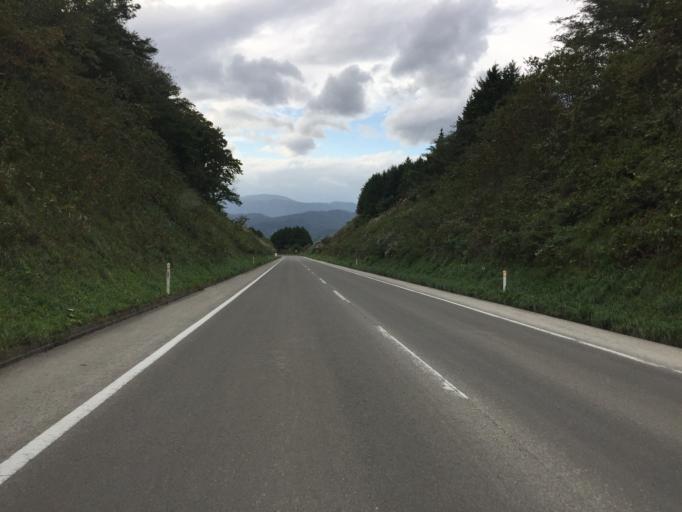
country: JP
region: Miyagi
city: Marumori
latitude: 37.9053
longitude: 140.7070
